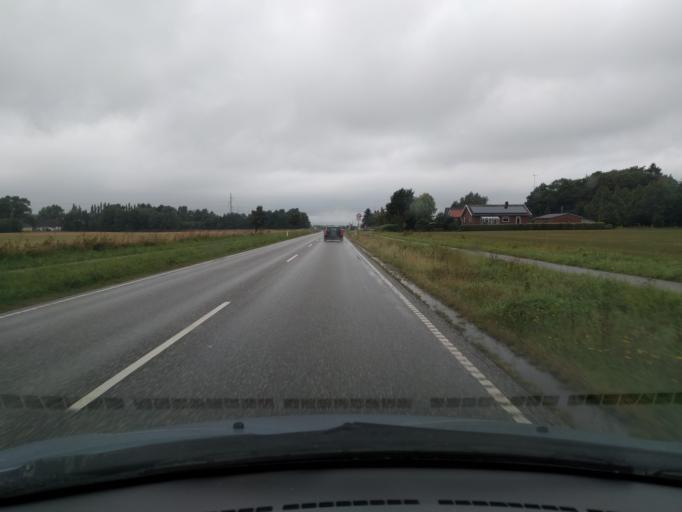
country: DK
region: Zealand
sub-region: Vordingborg Kommune
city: Neder Vindinge
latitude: 55.1100
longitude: 11.8202
